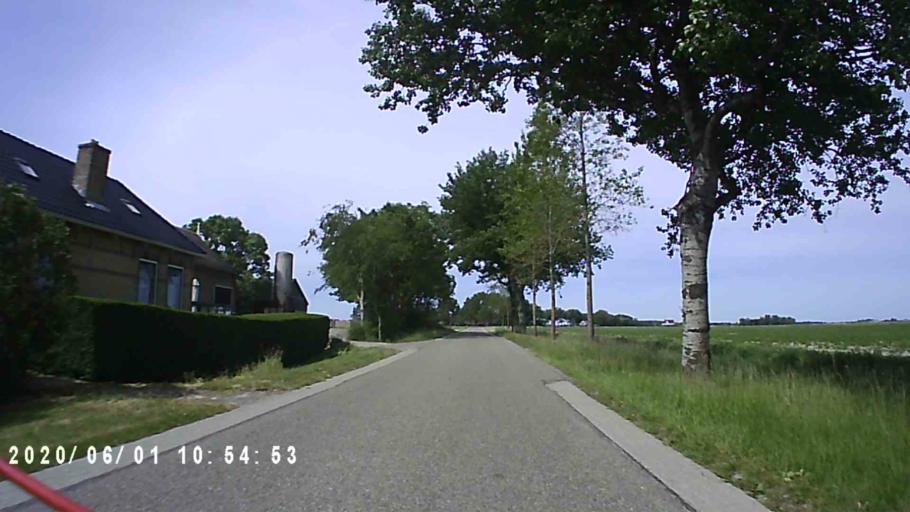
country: NL
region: Friesland
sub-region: Gemeente Franekeradeel
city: Sexbierum
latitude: 53.1999
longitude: 5.5086
